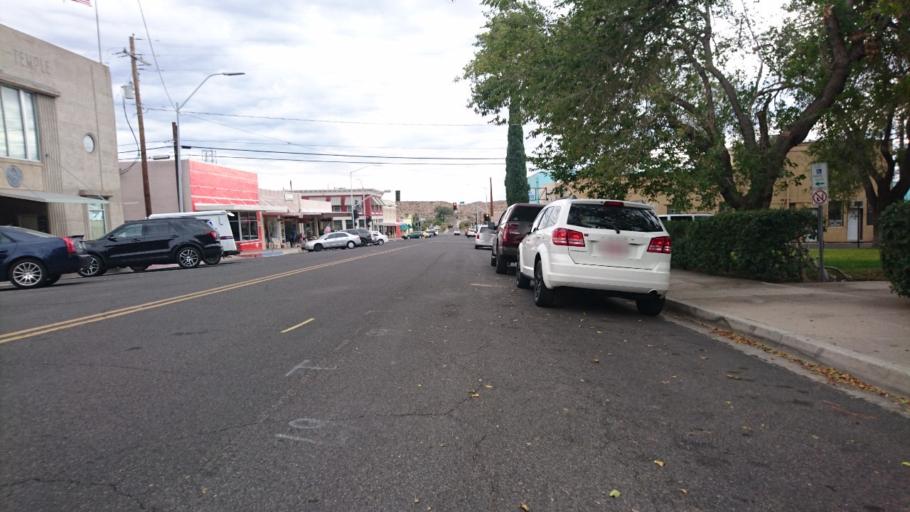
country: US
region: Arizona
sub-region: Mohave County
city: Kingman
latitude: 35.1904
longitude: -114.0529
